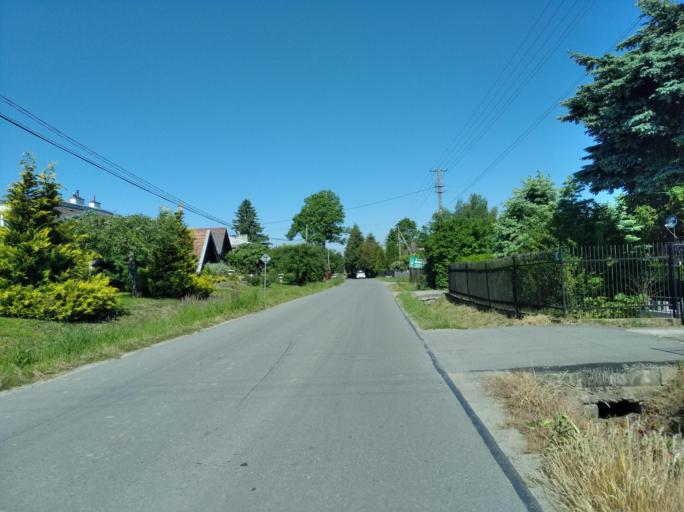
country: PL
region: Subcarpathian Voivodeship
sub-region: Powiat krosnienski
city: Korczyna
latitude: 49.7189
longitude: 21.7934
